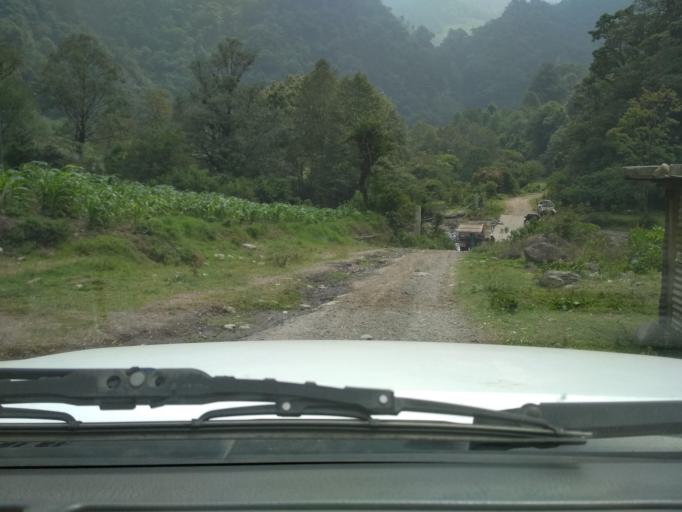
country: MX
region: Veracruz
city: Xocotla
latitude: 18.9910
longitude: -97.1038
